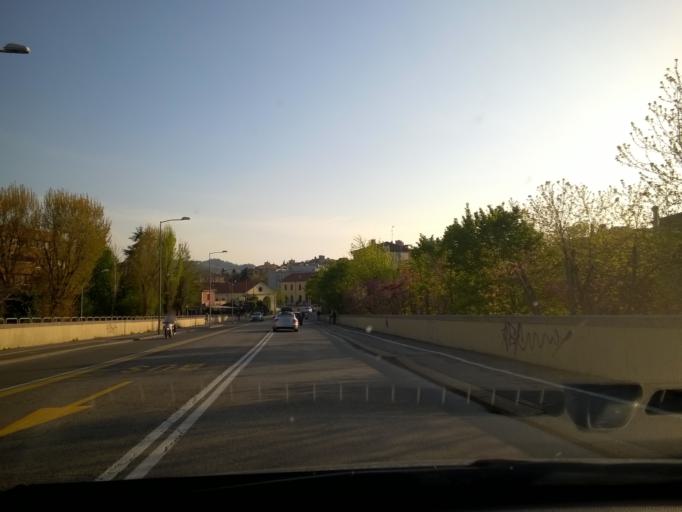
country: IT
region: Emilia-Romagna
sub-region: Provincia di Bologna
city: Bologna
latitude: 44.5006
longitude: 11.3602
